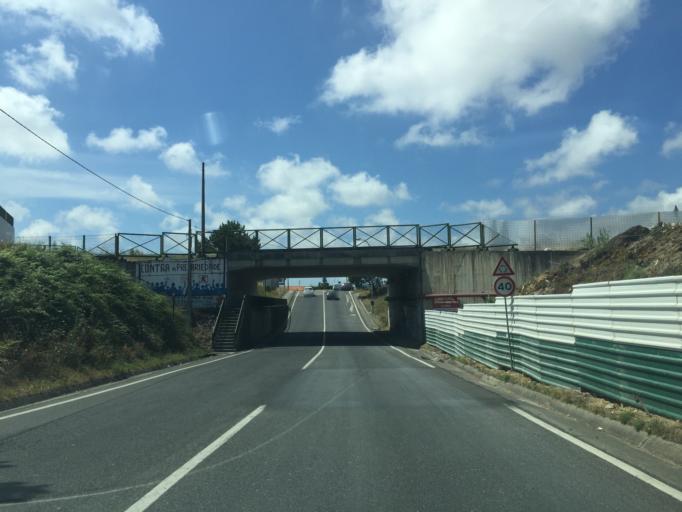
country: PT
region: Leiria
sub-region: Marinha Grande
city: Marinha Grande
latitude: 39.7339
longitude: -8.9309
